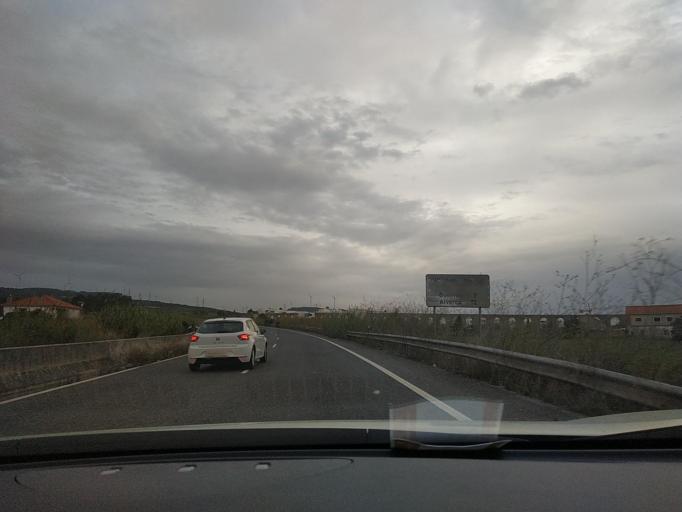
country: PT
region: Lisbon
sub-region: Loures
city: Santo Antao do Tojal
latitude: 38.8552
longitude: -9.1448
